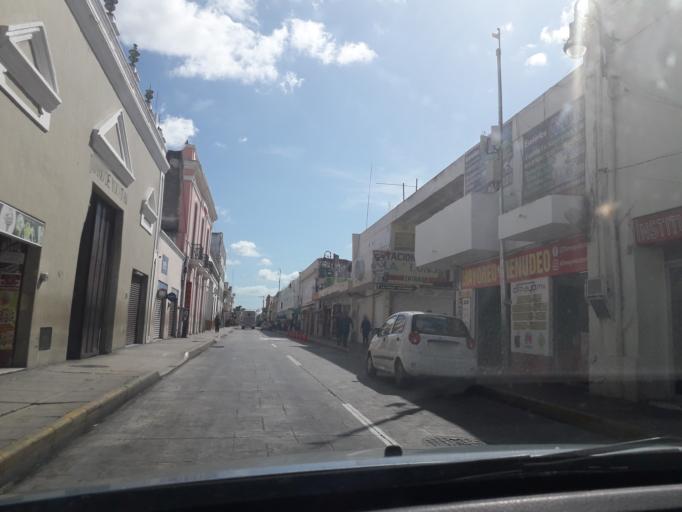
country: MX
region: Yucatan
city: Merida
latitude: 20.9649
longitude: -89.6247
